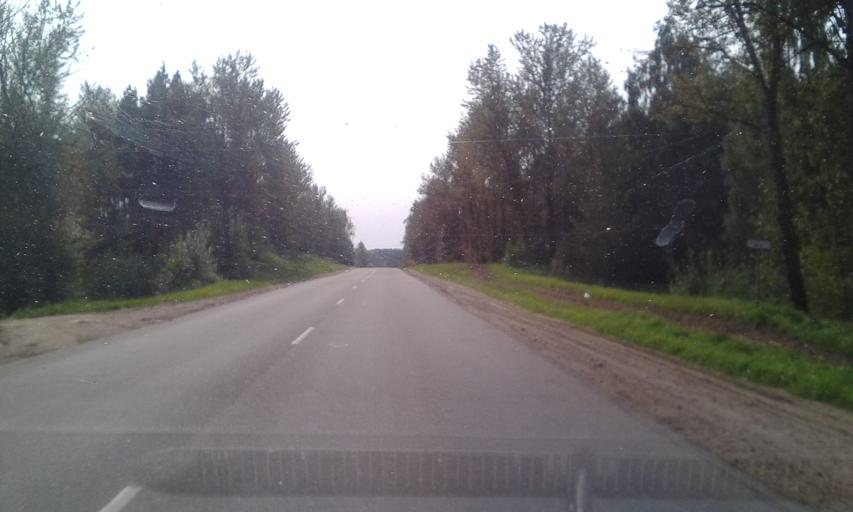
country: BY
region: Minsk
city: Hatava
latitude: 53.8106
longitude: 27.6469
